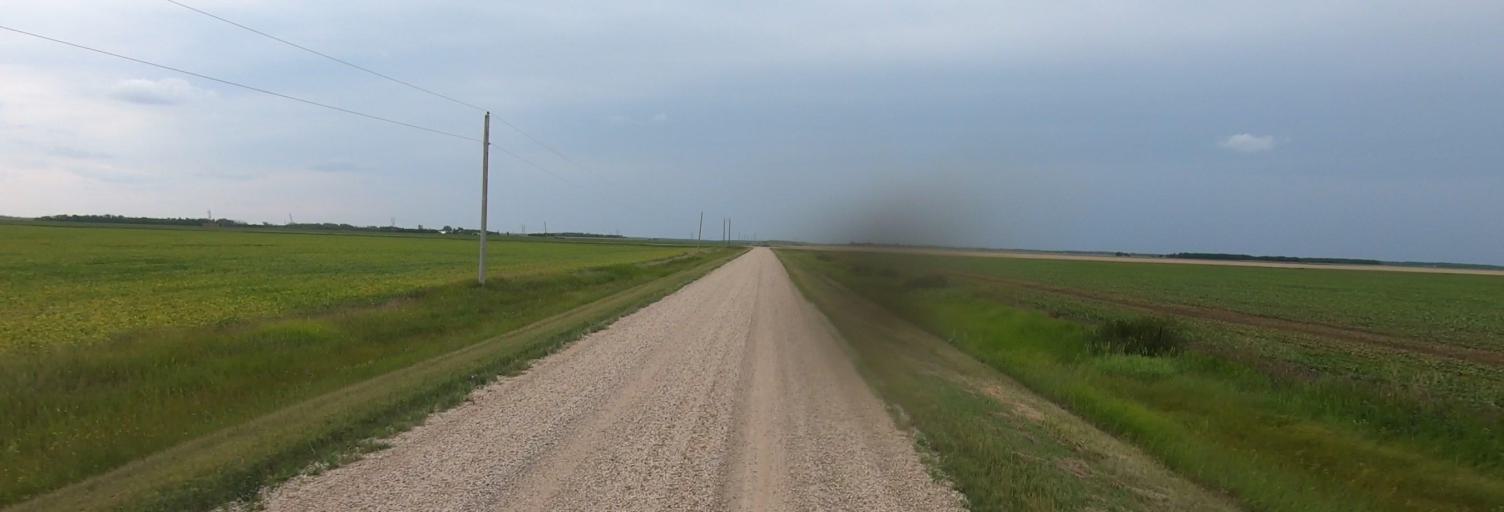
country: CA
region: Manitoba
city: Headingley
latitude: 49.7268
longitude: -97.4136
